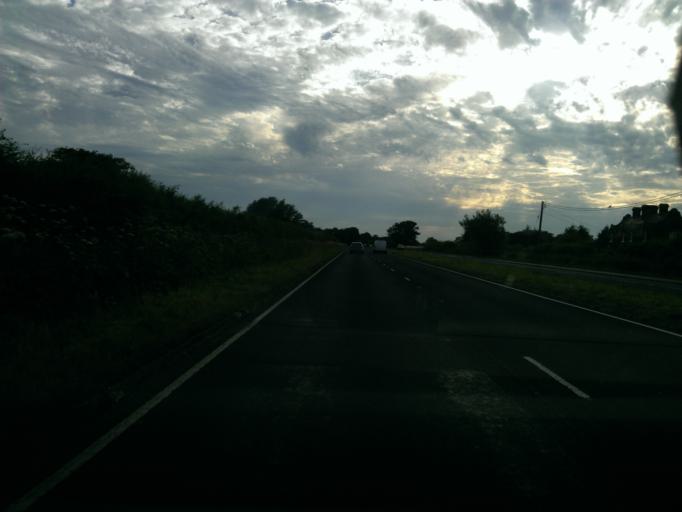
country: GB
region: England
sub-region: Essex
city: Wivenhoe
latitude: 51.8814
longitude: 0.9632
